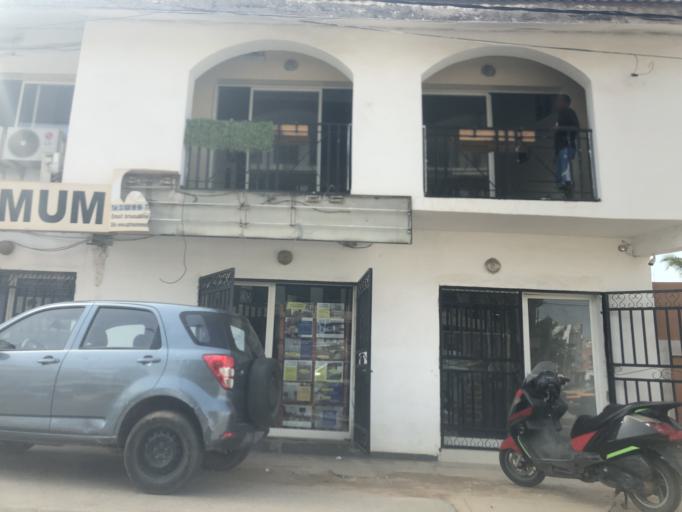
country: SN
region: Dakar
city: Mermoz Boabab
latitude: 14.7476
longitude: -17.5085
